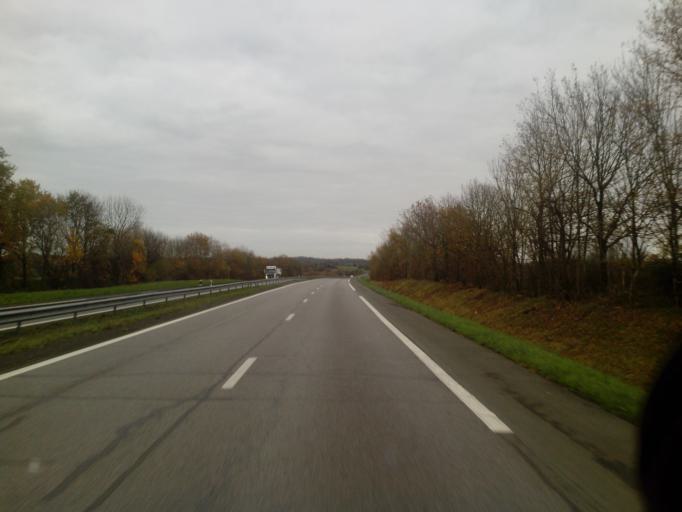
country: FR
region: Pays de la Loire
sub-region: Departement de Maine-et-Loire
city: Saint-Germain-sur-Moine
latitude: 47.1304
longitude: -1.1323
